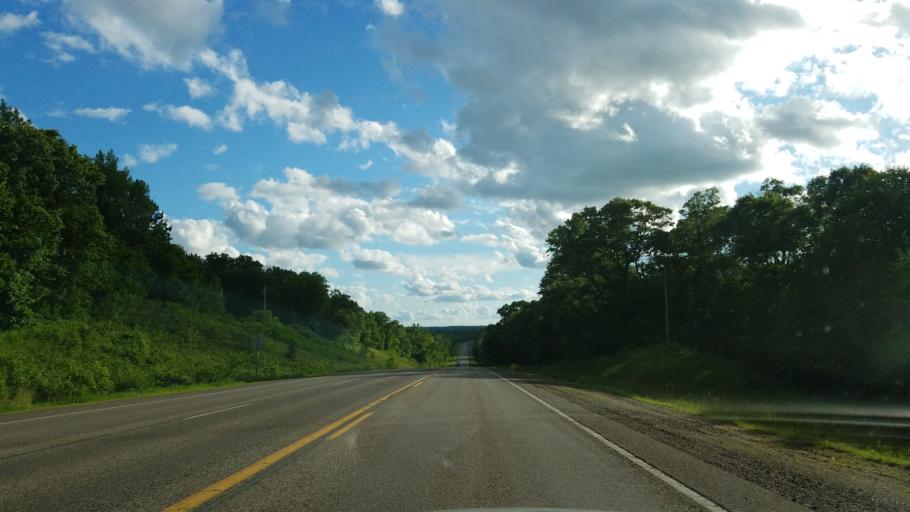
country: US
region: Wisconsin
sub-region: Polk County
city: Osceola
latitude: 45.3418
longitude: -92.6711
